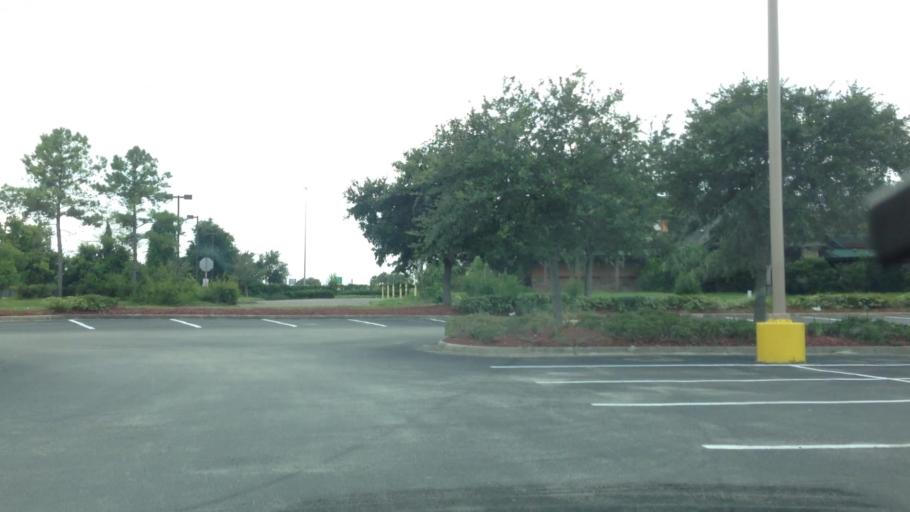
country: US
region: Florida
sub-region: Duval County
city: Jacksonville
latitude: 30.3311
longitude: -81.5505
